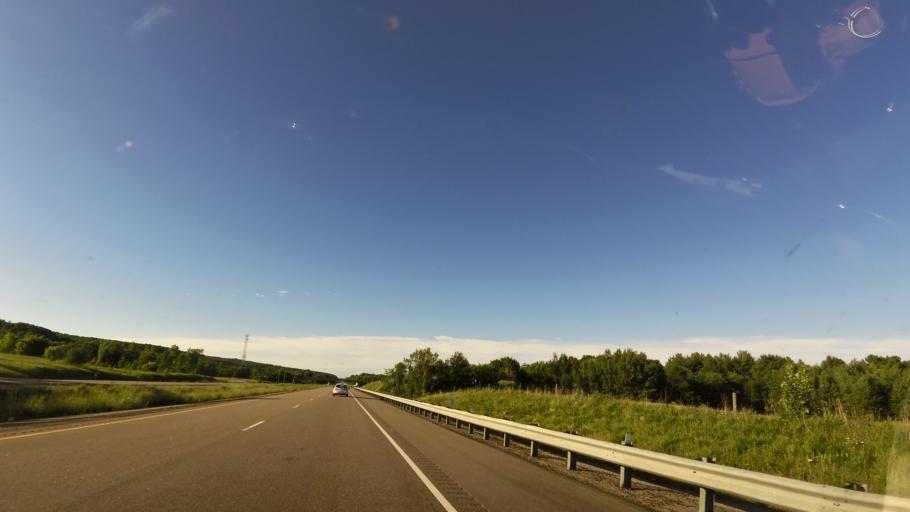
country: CA
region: Ontario
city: Barrie
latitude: 44.6200
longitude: -79.6618
